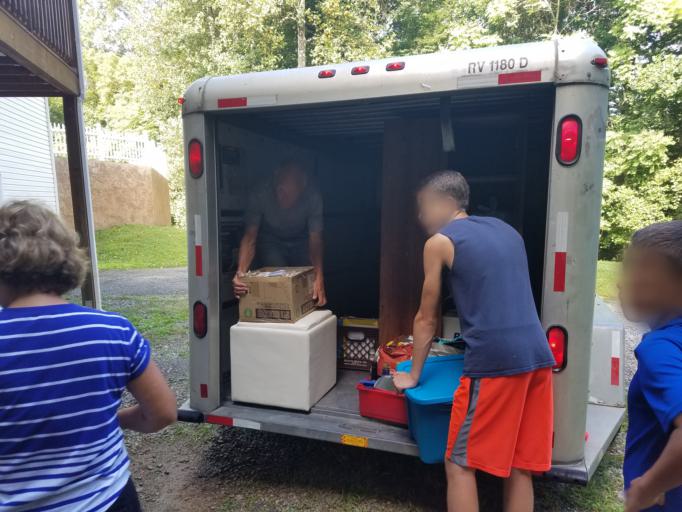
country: US
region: Virginia
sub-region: Franklin County
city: Henry Fork
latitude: 36.9576
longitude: -79.8894
